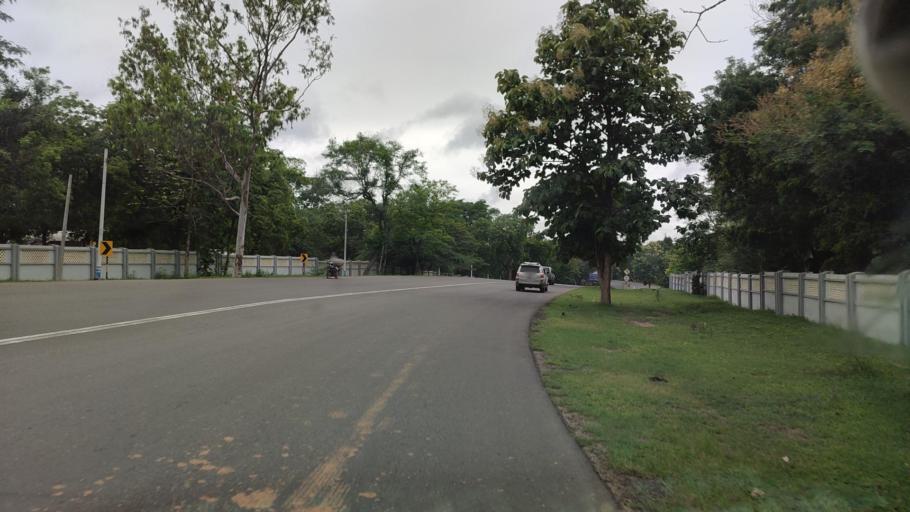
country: MM
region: Mandalay
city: Meiktila
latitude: 20.8519
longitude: 95.8830
